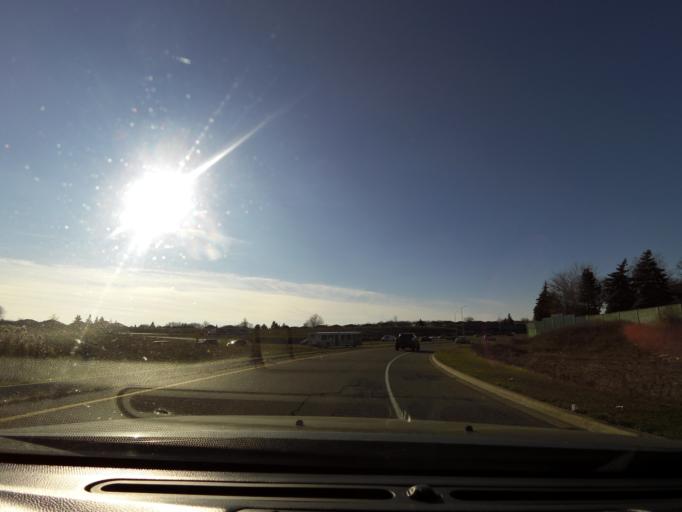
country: CA
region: Ontario
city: Hamilton
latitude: 43.2145
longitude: -79.8662
